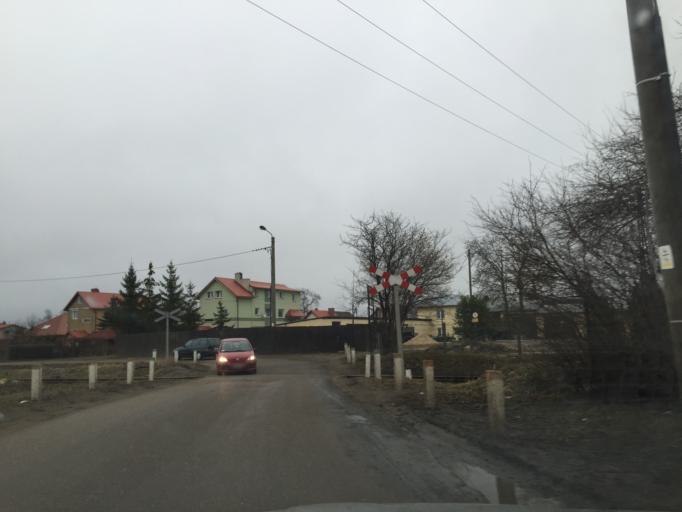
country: PL
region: Pomeranian Voivodeship
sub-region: Powiat kartuski
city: Chwaszczyno
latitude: 54.4154
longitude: 18.4474
